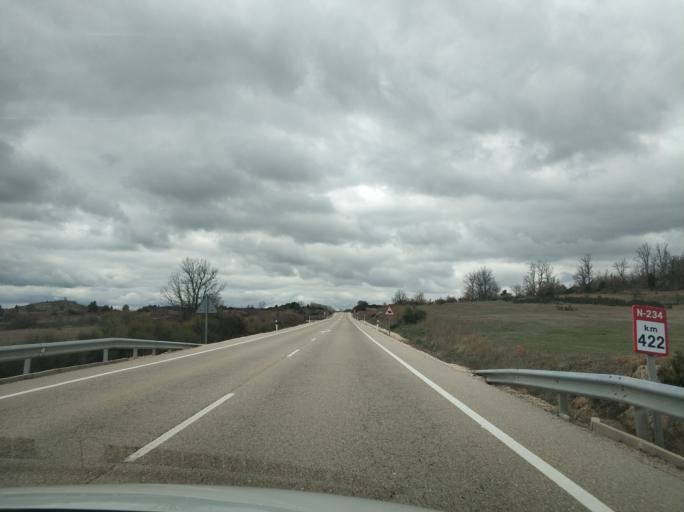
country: ES
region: Castille and Leon
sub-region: Provincia de Burgos
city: Cabezon de la Sierra
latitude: 41.8914
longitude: -3.2523
